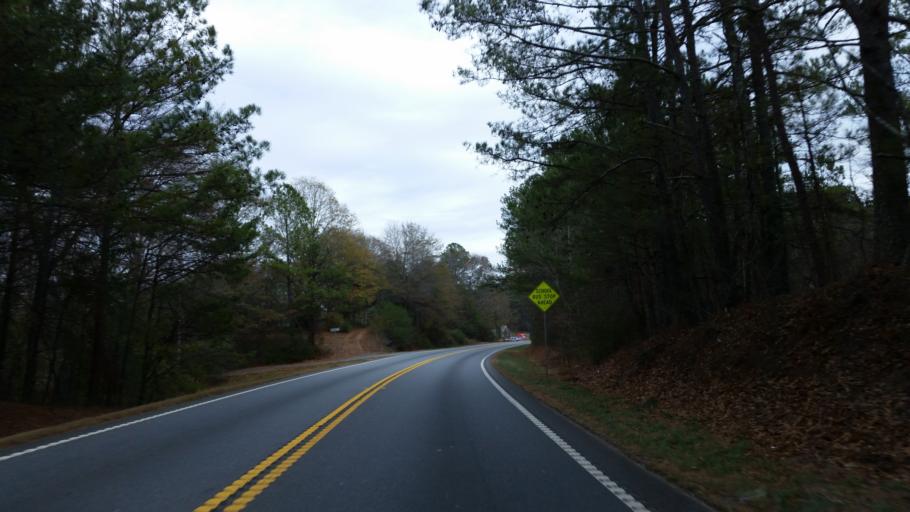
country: US
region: Georgia
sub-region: Cherokee County
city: Holly Springs
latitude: 34.2166
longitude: -84.6023
